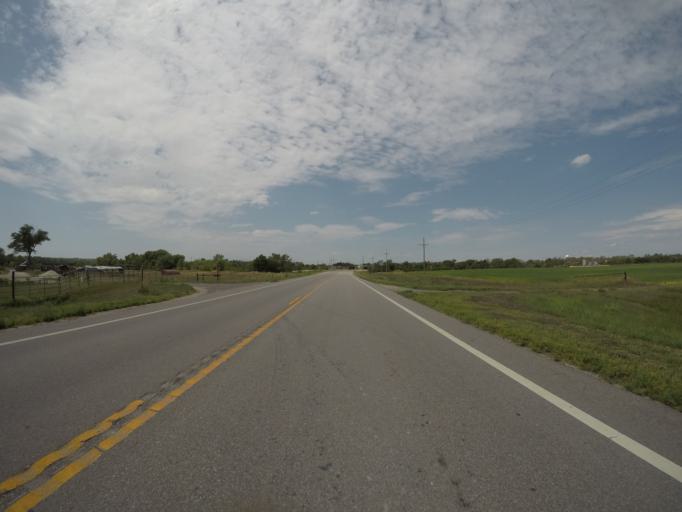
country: US
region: Kansas
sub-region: Rooks County
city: Stockton
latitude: 39.4380
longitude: -99.2557
